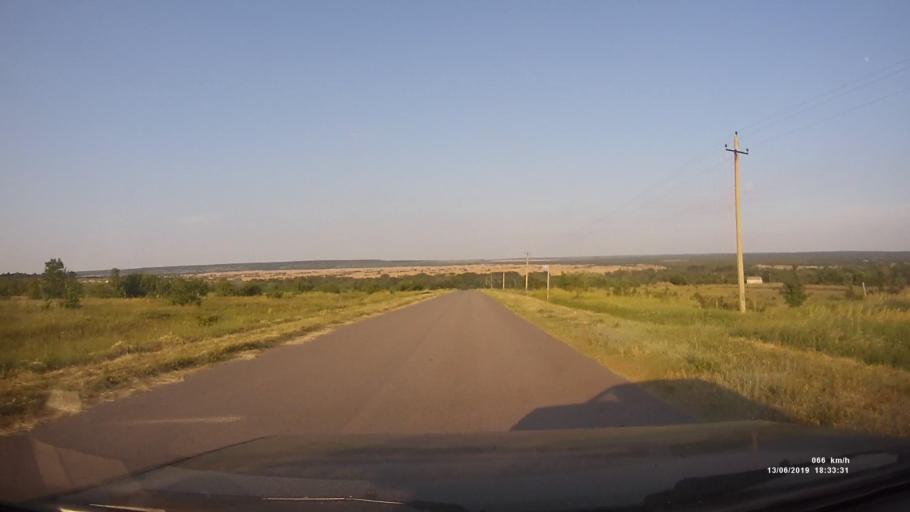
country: RU
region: Rostov
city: Kazanskaya
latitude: 49.8703
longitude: 41.3825
